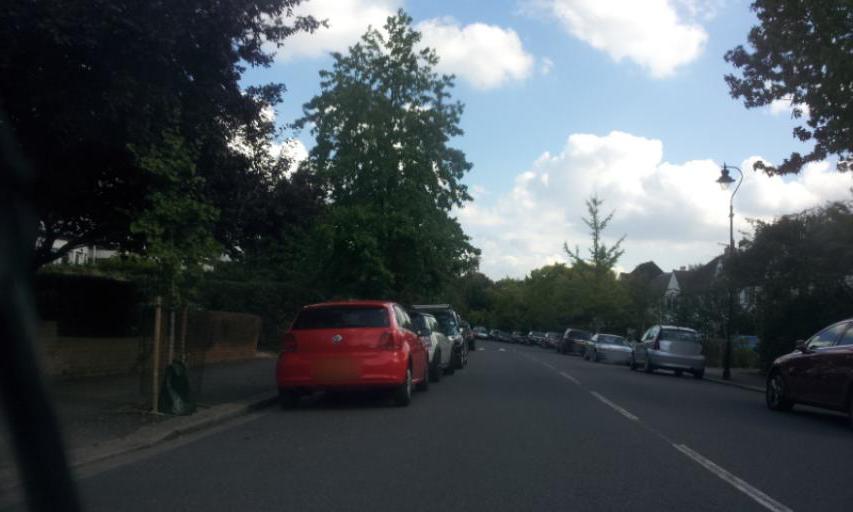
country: GB
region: England
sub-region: Greater London
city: Brixton
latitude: 51.4481
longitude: -0.0881
